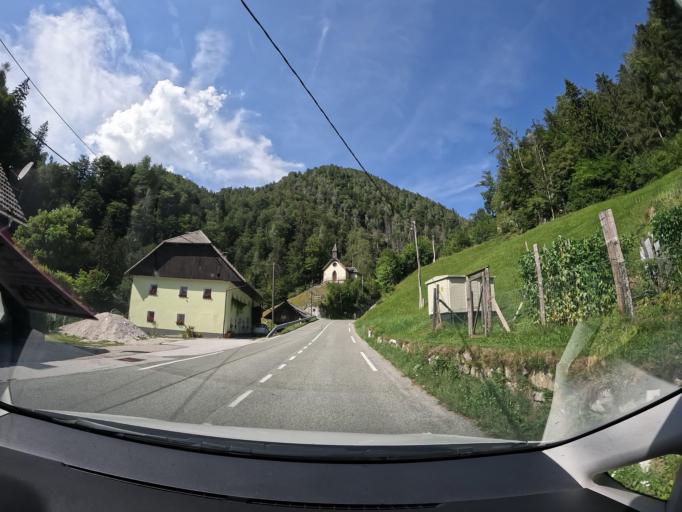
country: SI
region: Trzic
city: Trzic
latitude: 46.4113
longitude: 14.3008
